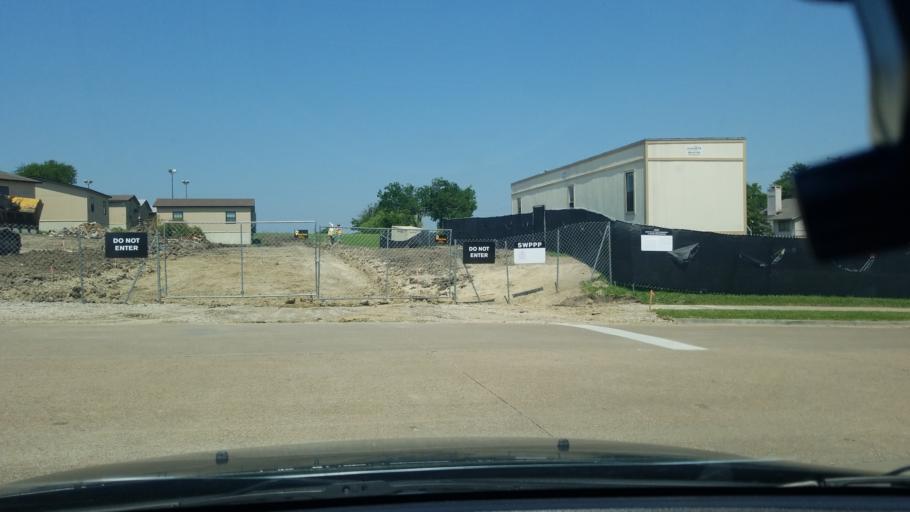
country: US
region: Texas
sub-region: Dallas County
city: Sunnyvale
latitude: 32.8284
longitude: -96.6026
